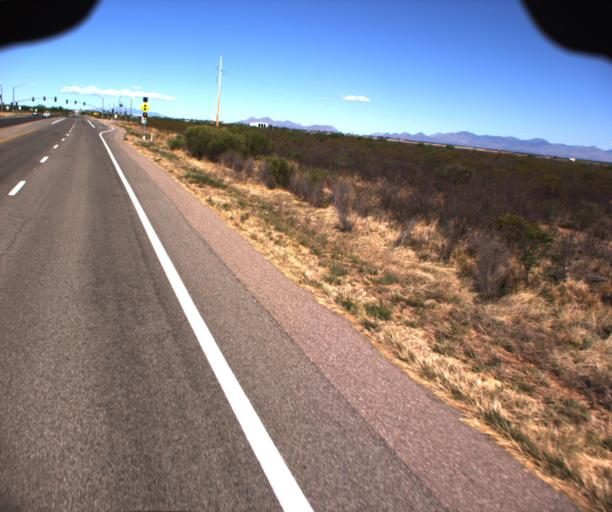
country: US
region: Arizona
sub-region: Cochise County
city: Sierra Vista Southeast
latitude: 31.5513
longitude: -110.1871
